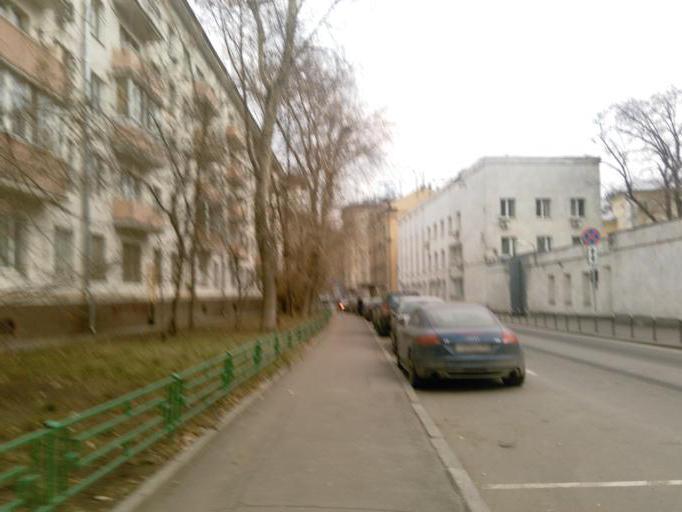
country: RU
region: Moskovskaya
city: Dorogomilovo
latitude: 55.7409
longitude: 37.5881
